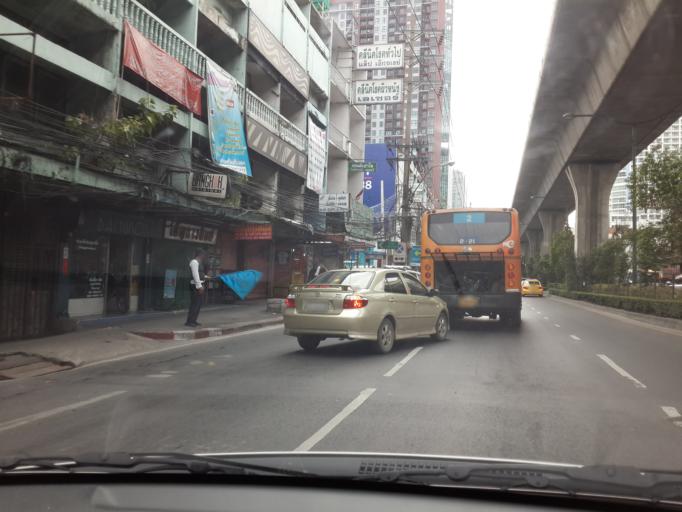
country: TH
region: Bangkok
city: Phra Khanong
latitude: 13.7117
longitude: 100.5958
